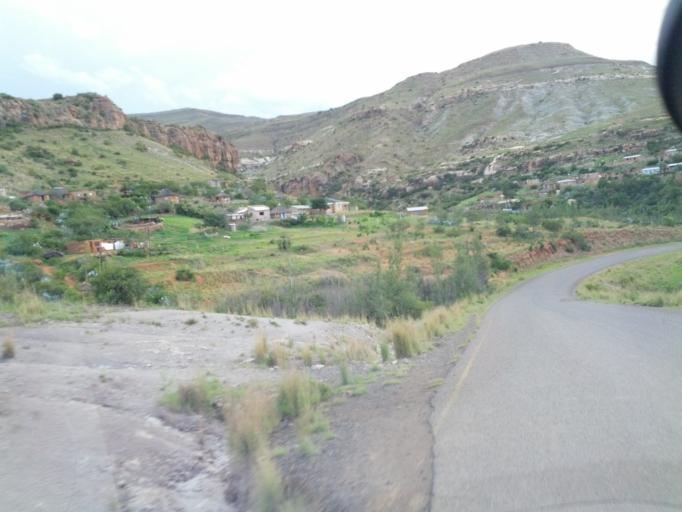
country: LS
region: Qacha's Nek
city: Qacha's Nek
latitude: -30.0735
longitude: 28.5624
